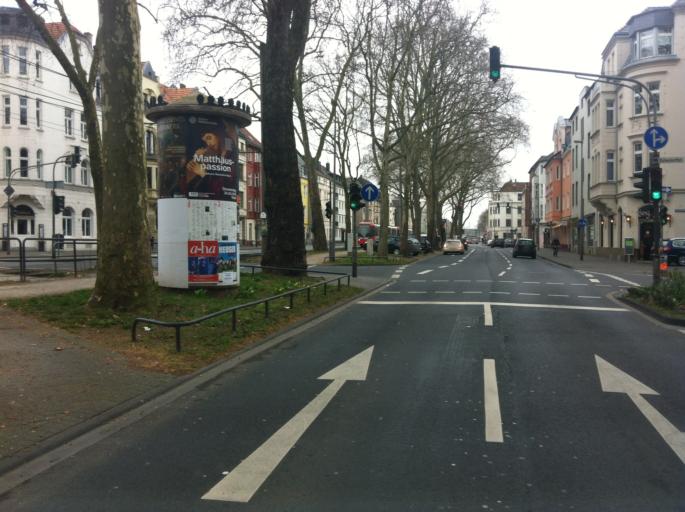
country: DE
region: North Rhine-Westphalia
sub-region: Regierungsbezirk Koln
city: Neuehrenfeld
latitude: 50.9564
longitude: 6.9227
